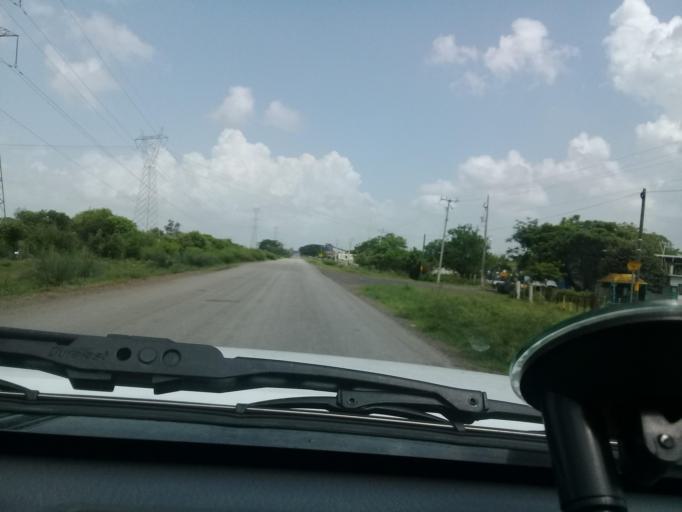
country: MX
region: Veracruz
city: Moralillo
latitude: 22.2236
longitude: -98.0088
